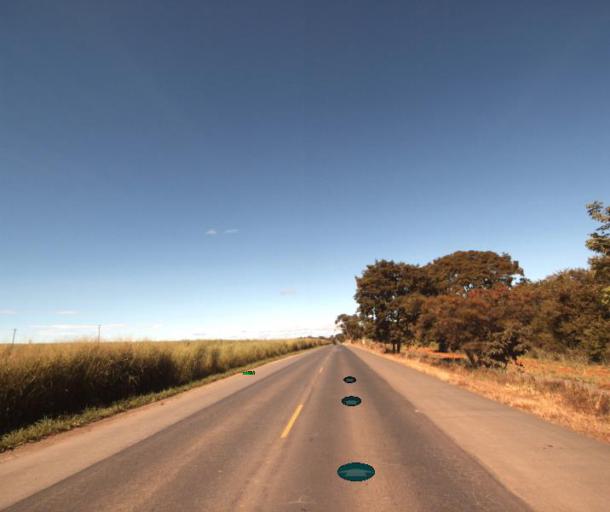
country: BR
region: Goias
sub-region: Itapaci
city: Itapaci
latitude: -14.9780
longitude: -49.3956
